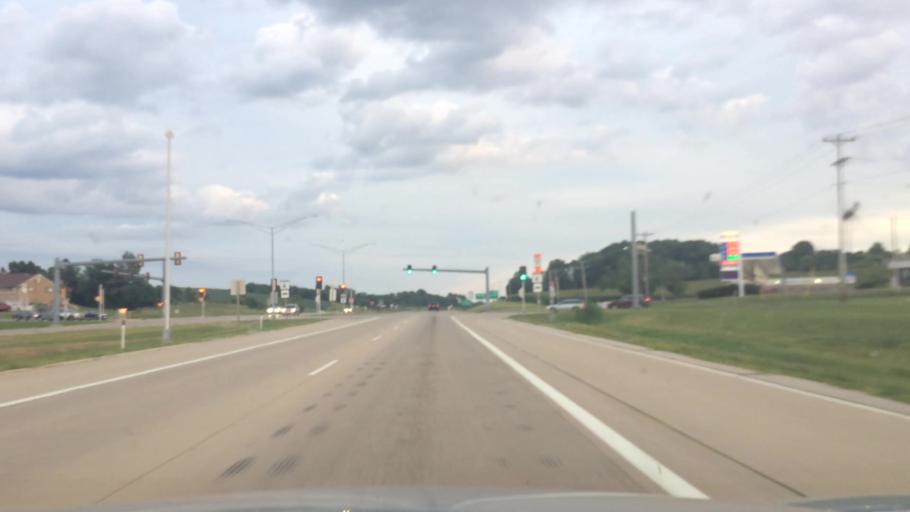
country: US
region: Wisconsin
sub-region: Dane County
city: Middleton
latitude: 43.1415
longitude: -89.5208
